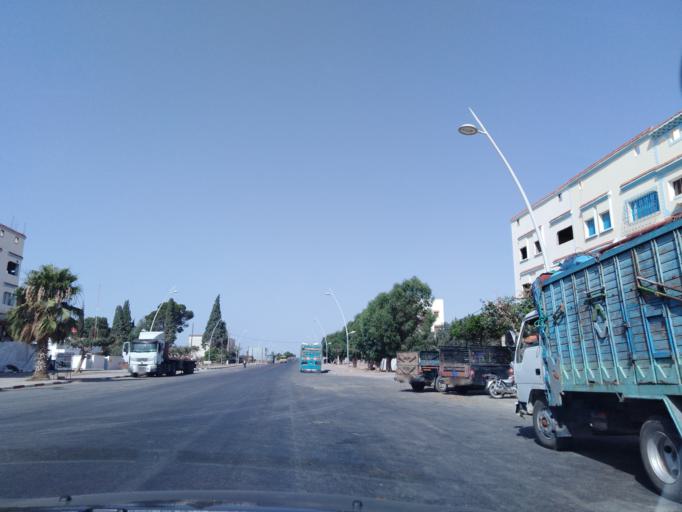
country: MA
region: Doukkala-Abda
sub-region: Safi
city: Safi
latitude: 32.2549
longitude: -8.9803
